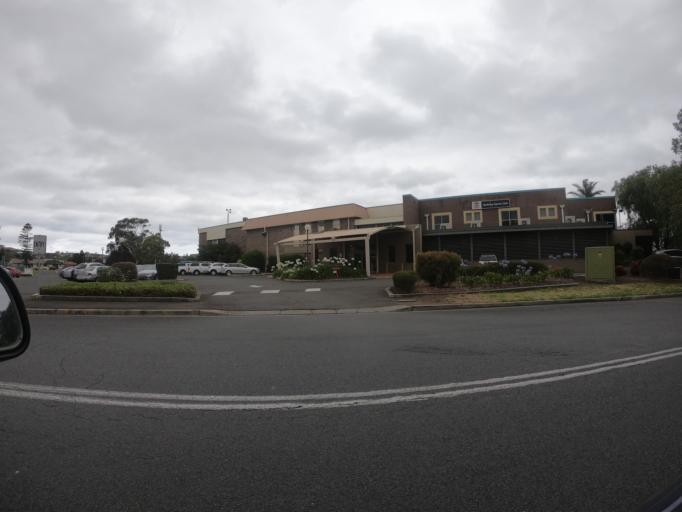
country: AU
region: New South Wales
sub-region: Wollongong
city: Berkeley
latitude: -34.4821
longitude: 150.8471
